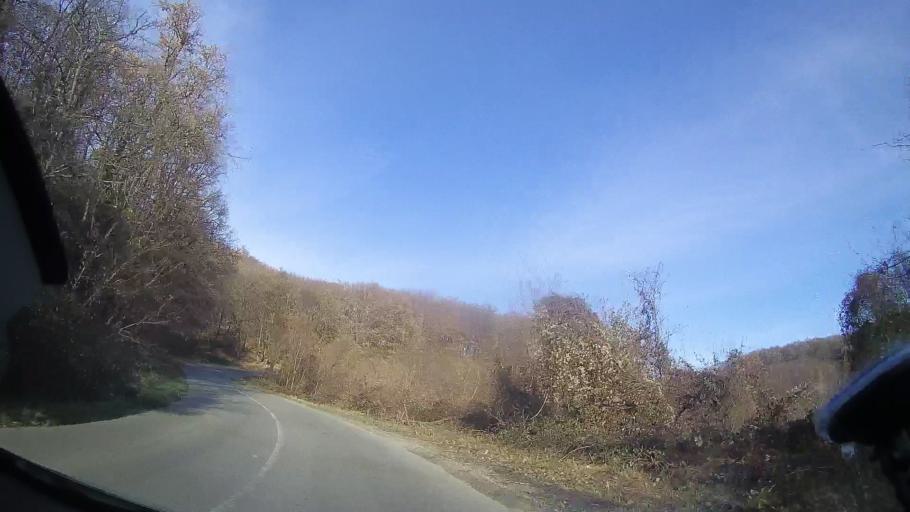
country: RO
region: Bihor
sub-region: Comuna Tileagd
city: Tileagd
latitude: 47.0977
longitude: 22.2416
